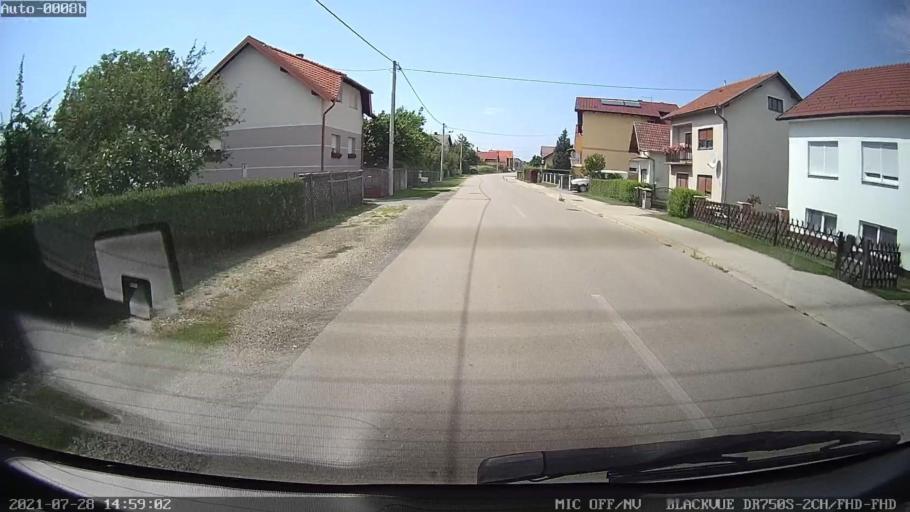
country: HR
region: Varazdinska
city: Varazdin
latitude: 46.2870
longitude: 16.3814
